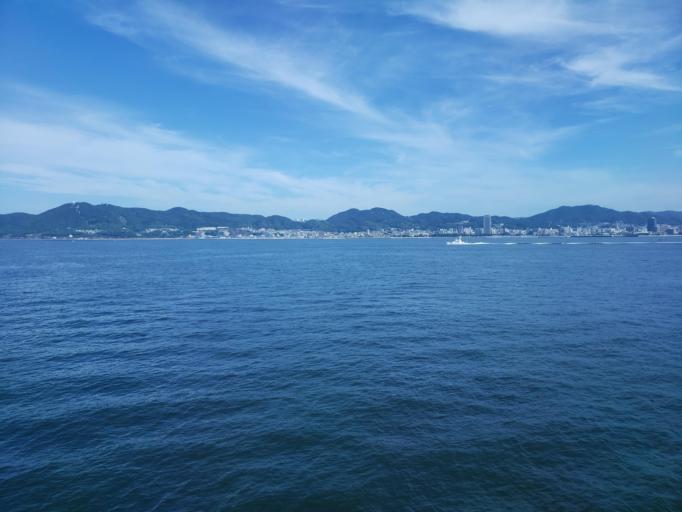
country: JP
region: Hyogo
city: Kobe
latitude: 34.6181
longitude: 135.1309
